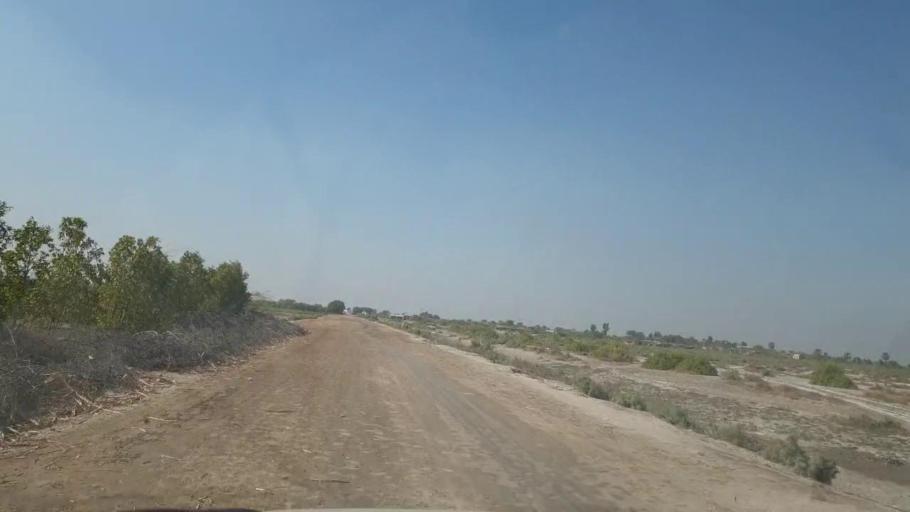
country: PK
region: Sindh
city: Mirpur Khas
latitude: 25.4758
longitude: 69.1212
